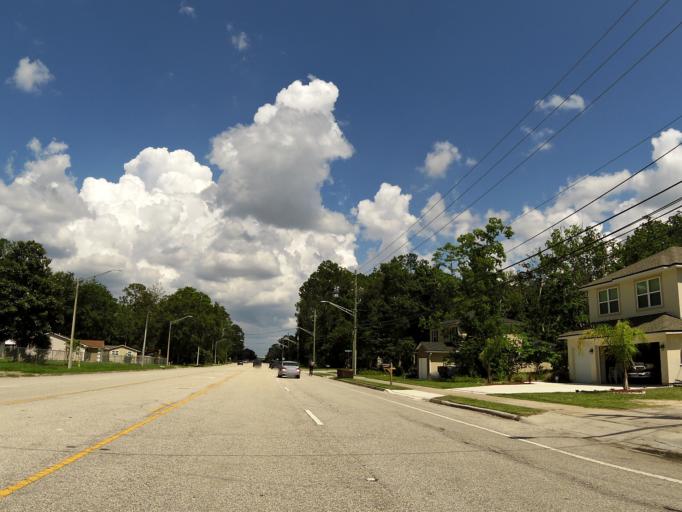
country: US
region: Florida
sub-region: Saint Johns County
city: Fruit Cove
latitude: 30.1467
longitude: -81.5681
